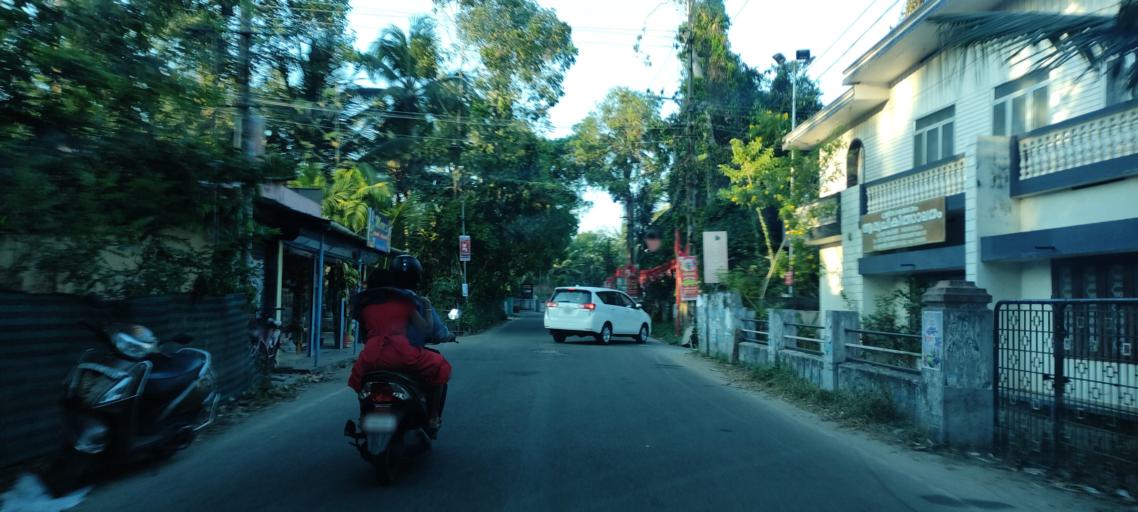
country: IN
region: Kerala
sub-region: Alappuzha
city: Kayankulam
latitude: 9.1844
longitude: 76.4719
